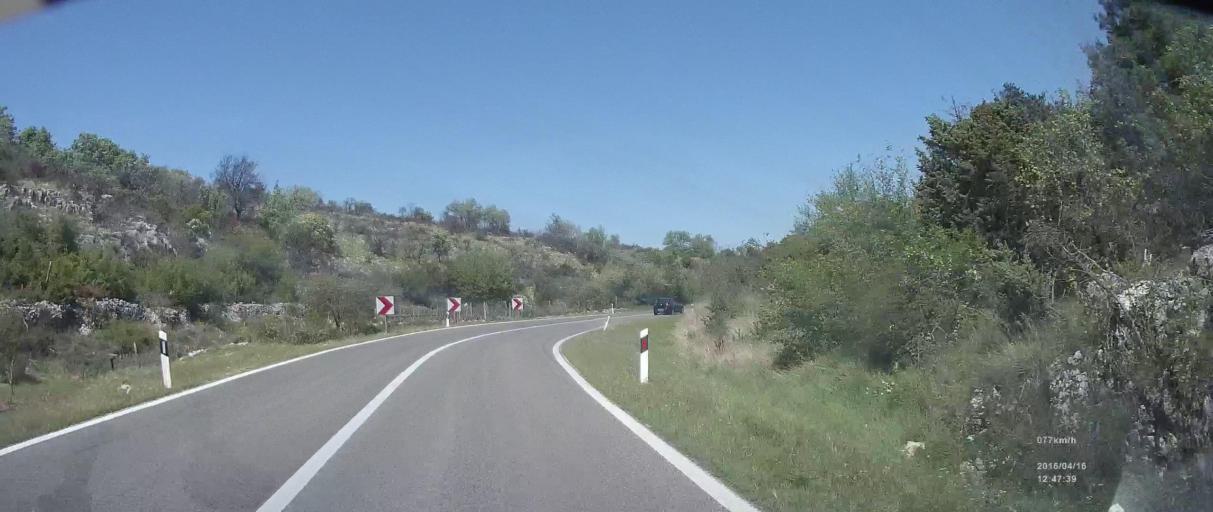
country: HR
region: Sibensko-Kniniska
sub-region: Grad Sibenik
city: Brodarica
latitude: 43.6661
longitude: 16.0445
